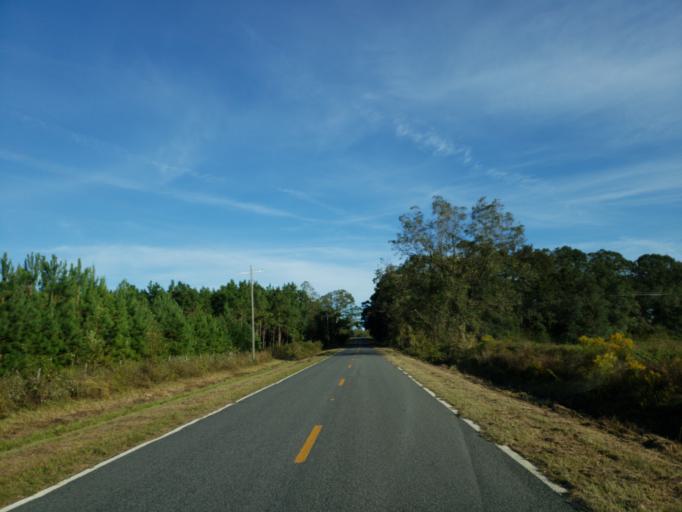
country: US
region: Georgia
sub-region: Crisp County
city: Cordele
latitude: 32.0309
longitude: -83.7475
